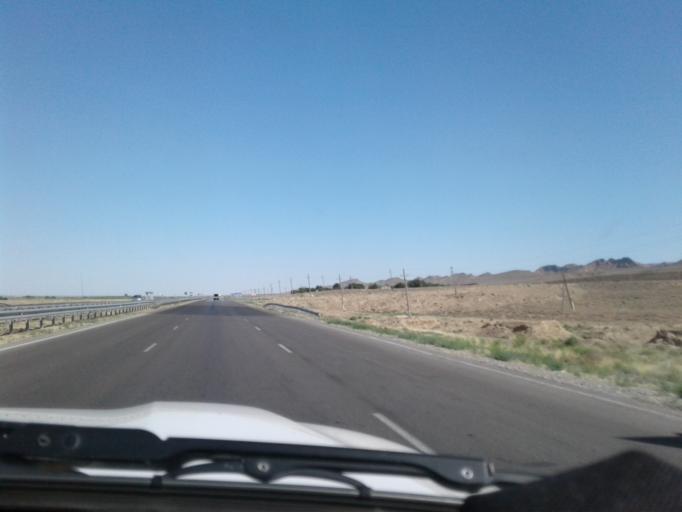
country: IR
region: Razavi Khorasan
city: Dargaz
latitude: 37.6452
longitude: 59.1372
